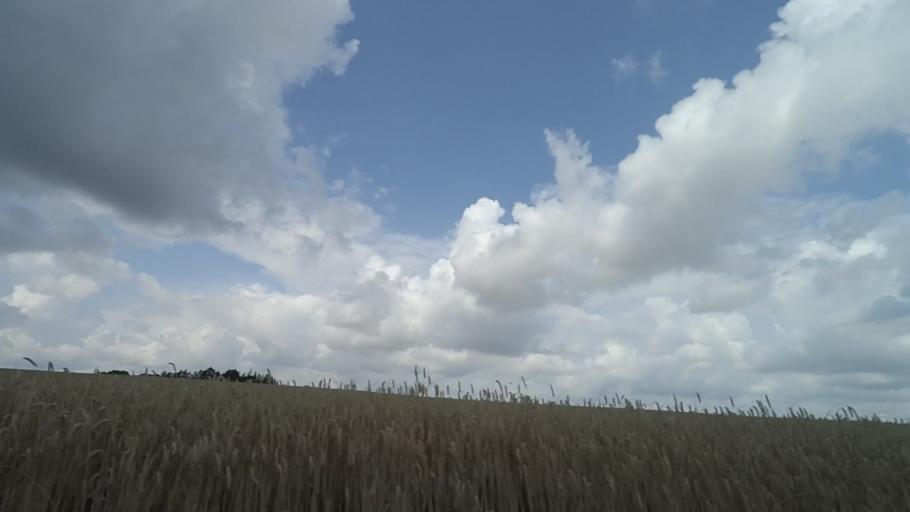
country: DK
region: Central Jutland
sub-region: Norddjurs Kommune
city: Allingabro
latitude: 56.4985
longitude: 10.3716
